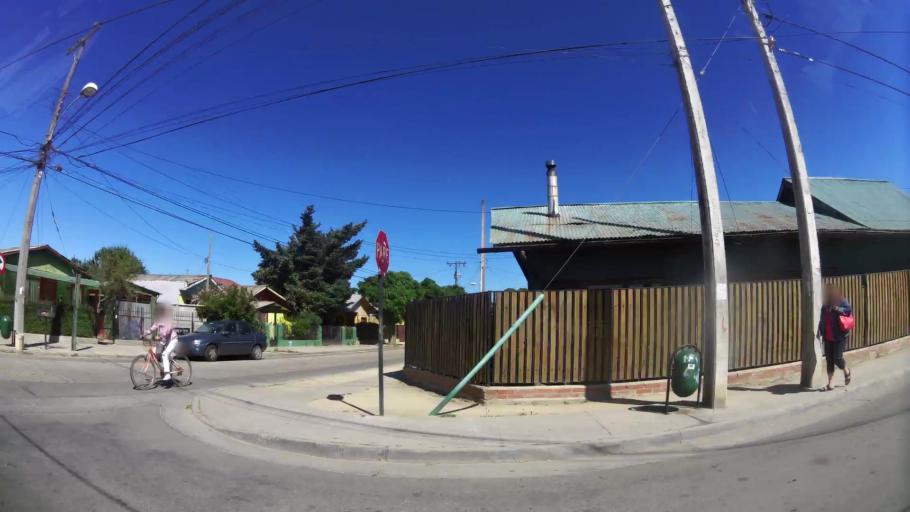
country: CL
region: Valparaiso
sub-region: Provincia de Marga Marga
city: Quilpue
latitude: -33.3182
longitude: -71.4070
